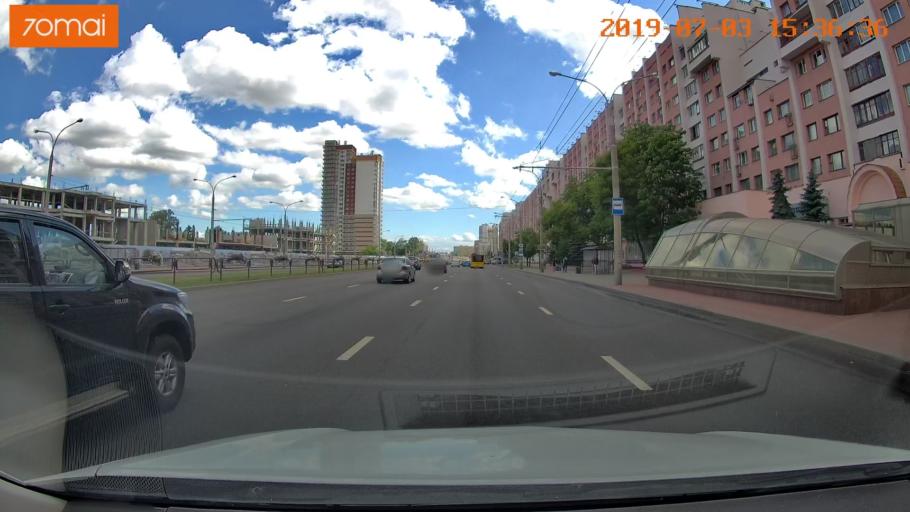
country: BY
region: Minsk
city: Minsk
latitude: 53.8821
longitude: 27.5680
